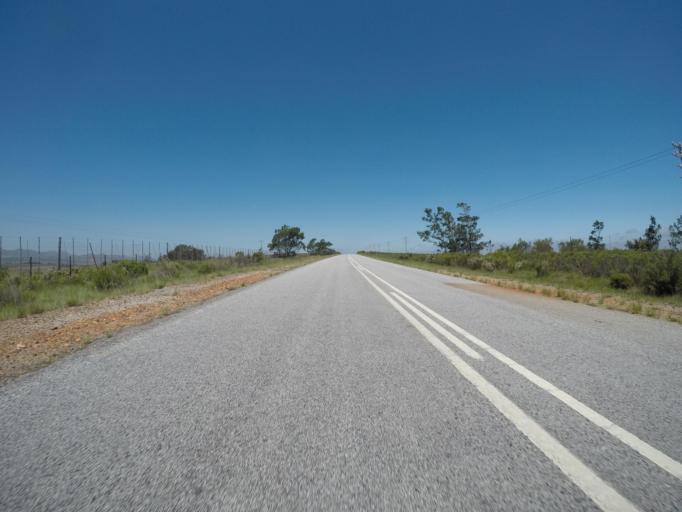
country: ZA
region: Eastern Cape
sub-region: Cacadu District Municipality
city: Kruisfontein
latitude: -33.9892
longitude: 24.5274
